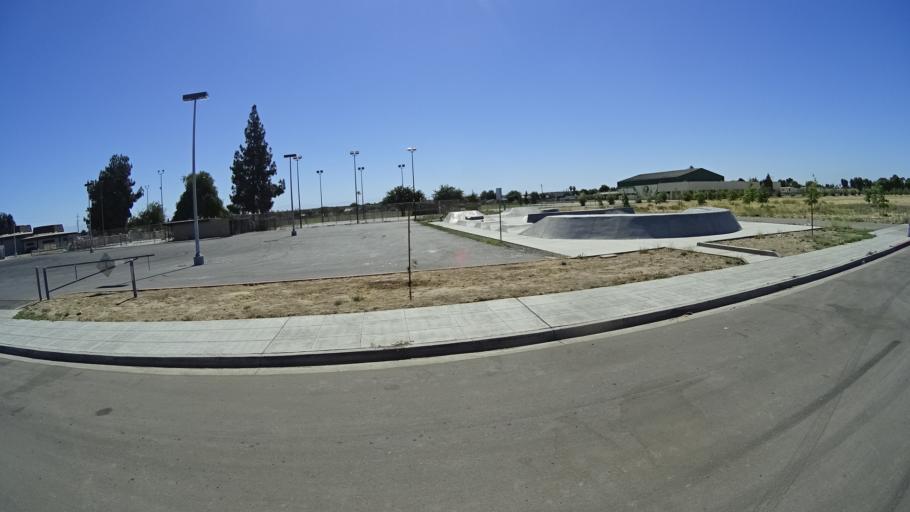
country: US
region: California
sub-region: Fresno County
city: Easton
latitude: 36.6978
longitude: -119.7966
